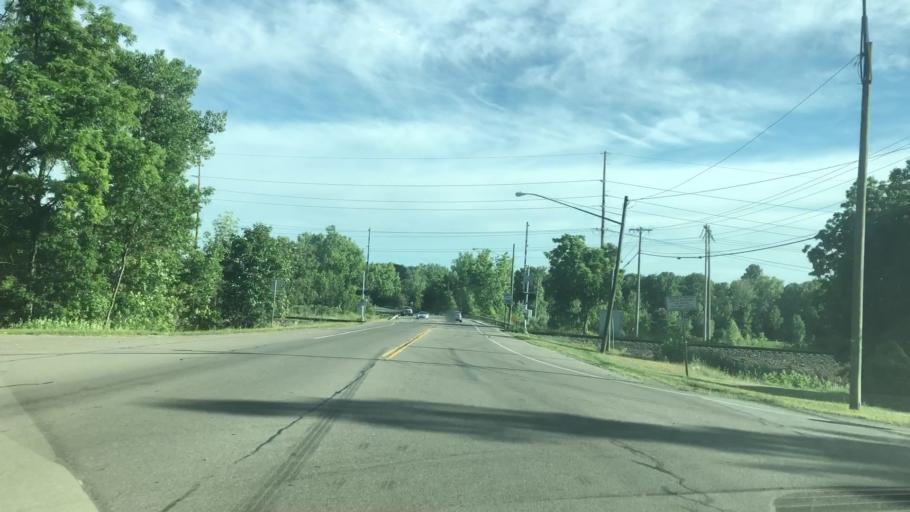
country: US
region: New York
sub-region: Wayne County
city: Macedon
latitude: 43.0768
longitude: -77.3014
